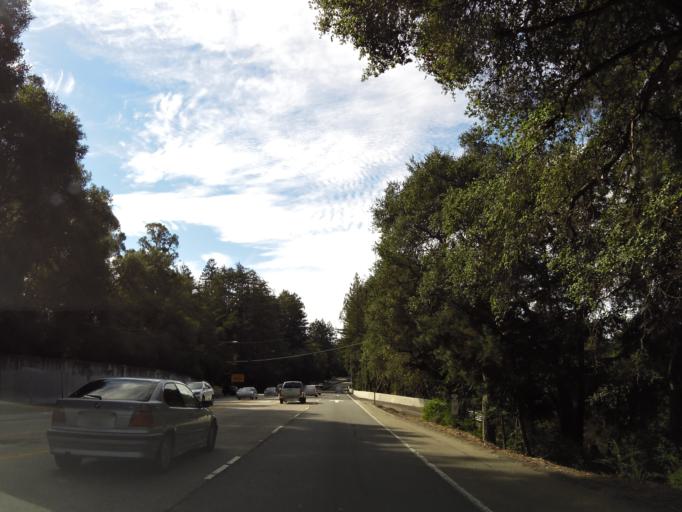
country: US
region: California
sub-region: Santa Cruz County
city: Scotts Valley
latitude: 37.0798
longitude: -121.9786
